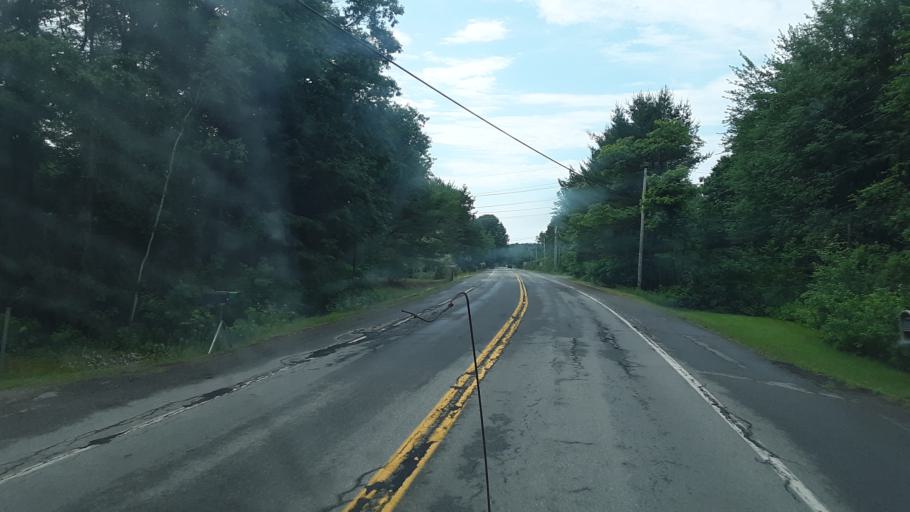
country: US
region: Maine
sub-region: Penobscot County
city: Eddington
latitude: 44.8332
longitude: -68.6956
